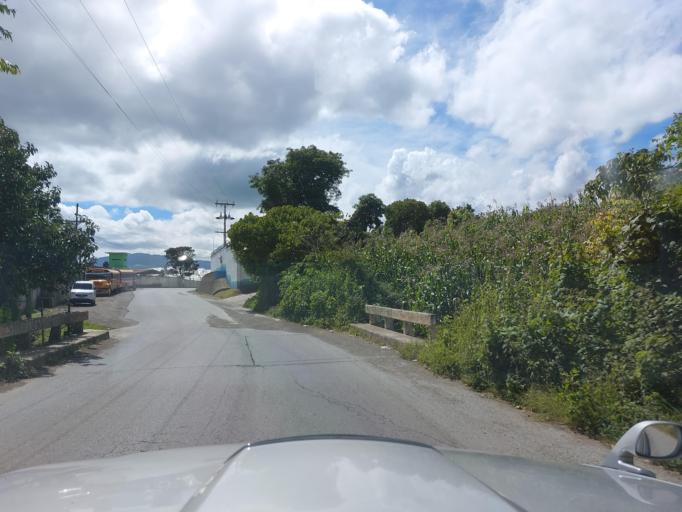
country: GT
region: Chimaltenango
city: Parramos
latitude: 14.6107
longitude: -90.8161
